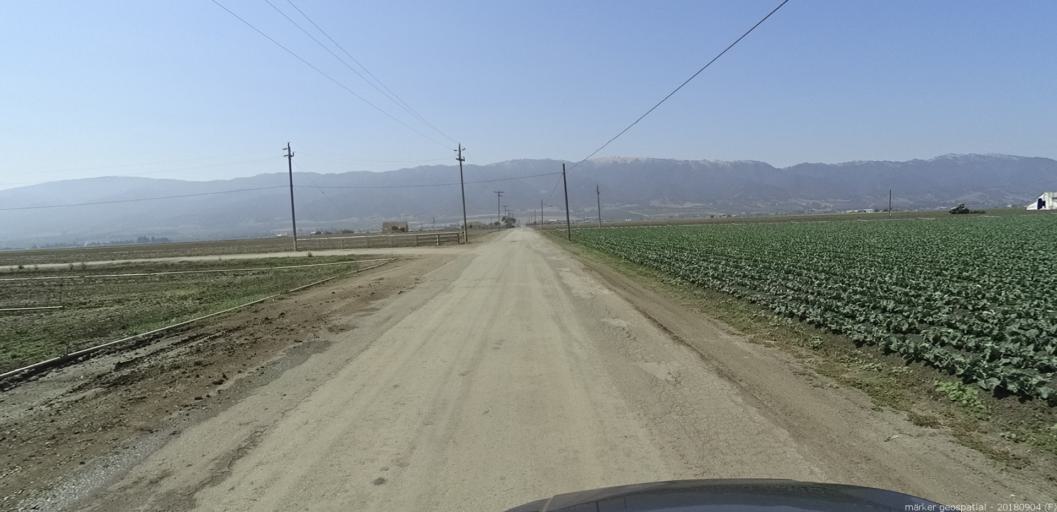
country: US
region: California
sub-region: Monterey County
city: Gonzales
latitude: 36.5143
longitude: -121.4665
